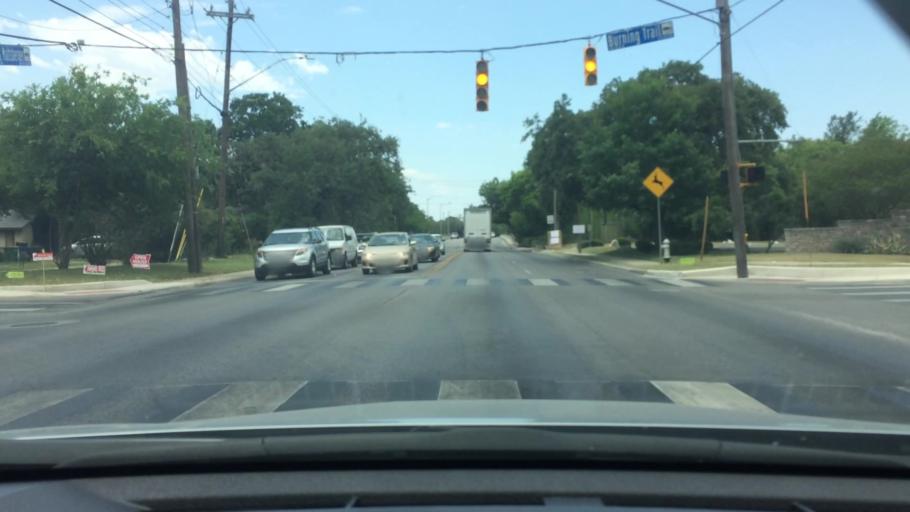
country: US
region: Texas
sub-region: Bexar County
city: Hollywood Park
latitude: 29.5703
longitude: -98.4501
